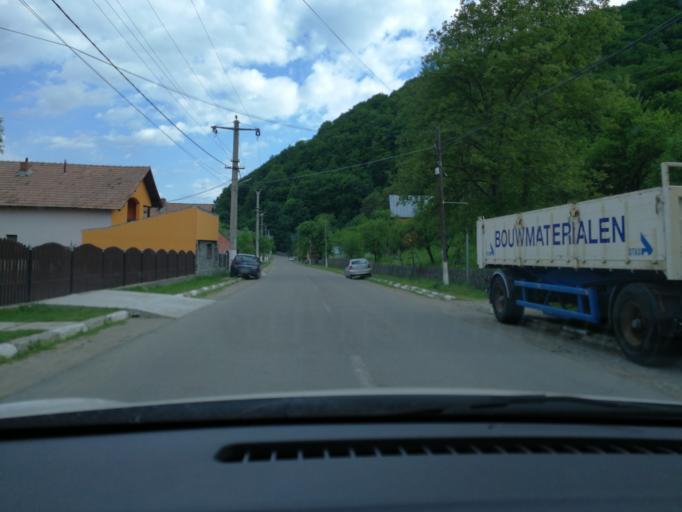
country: RO
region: Prahova
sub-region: Comuna Valea Doftanei
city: Tesila
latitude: 45.2854
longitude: 25.7233
